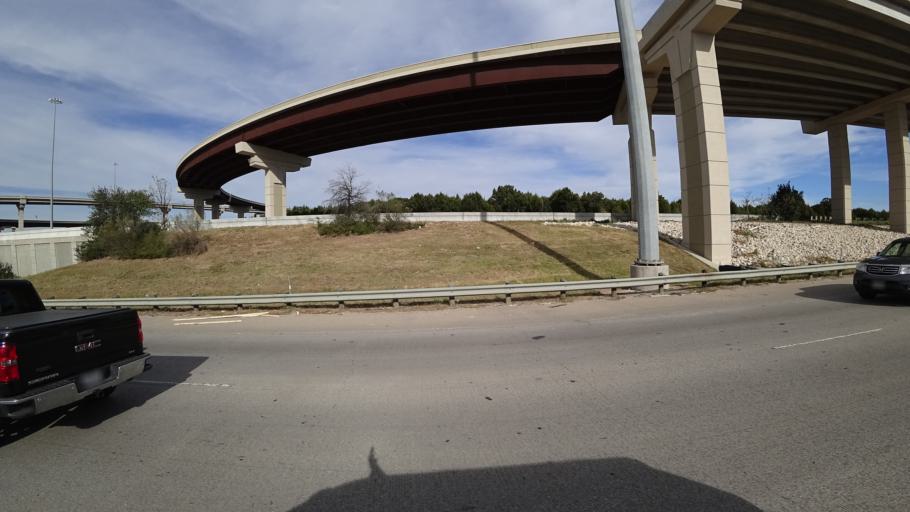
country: US
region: Texas
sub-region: Travis County
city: Austin
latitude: 30.3237
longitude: -97.6706
